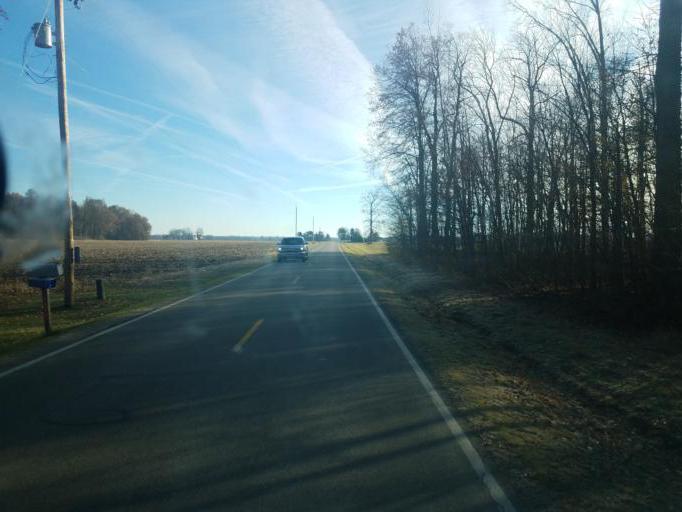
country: US
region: Ohio
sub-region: Crawford County
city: Galion
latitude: 40.7331
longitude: -82.8901
